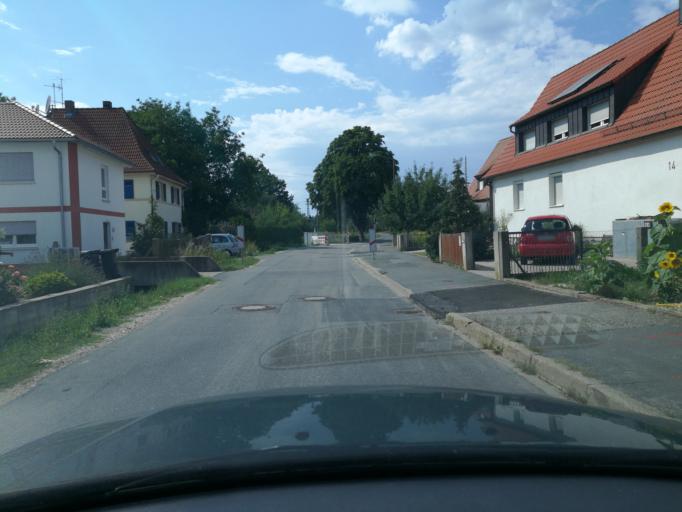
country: DE
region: Bavaria
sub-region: Regierungsbezirk Mittelfranken
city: Erlangen
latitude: 49.5351
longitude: 10.9984
